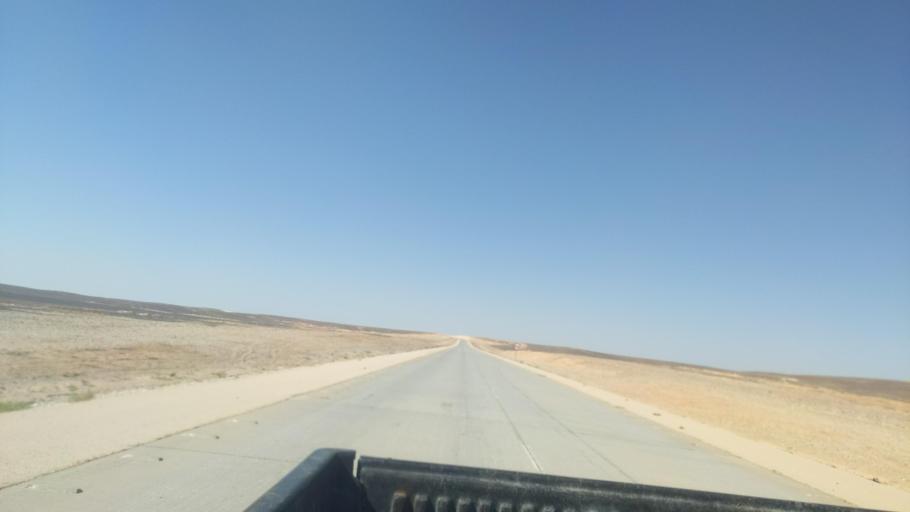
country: JO
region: Amman
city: Al Azraq ash Shamali
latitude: 31.4030
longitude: 36.7132
